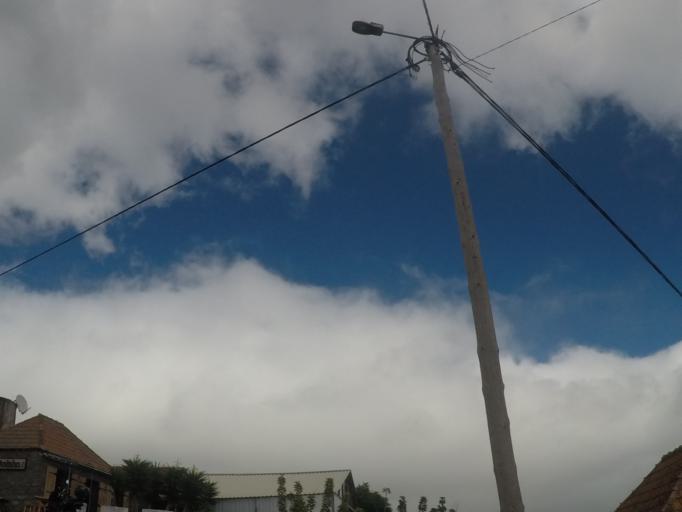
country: PT
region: Madeira
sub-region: Santa Cruz
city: Camacha
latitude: 32.6628
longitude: -16.8249
